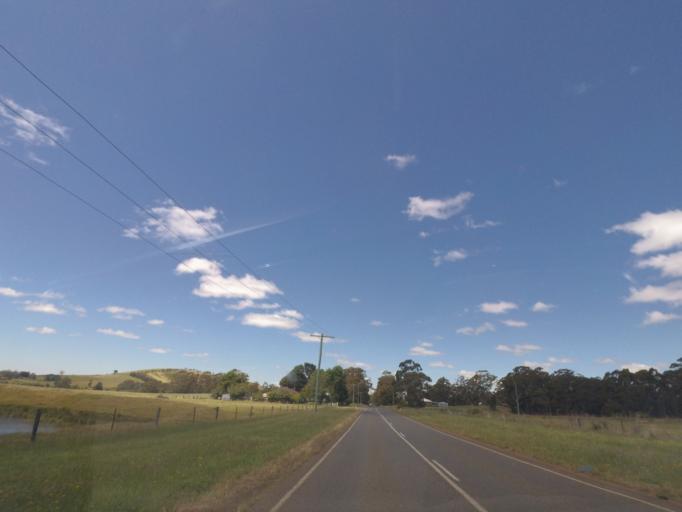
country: AU
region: Victoria
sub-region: Mount Alexander
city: Castlemaine
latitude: -37.3197
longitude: 144.2075
